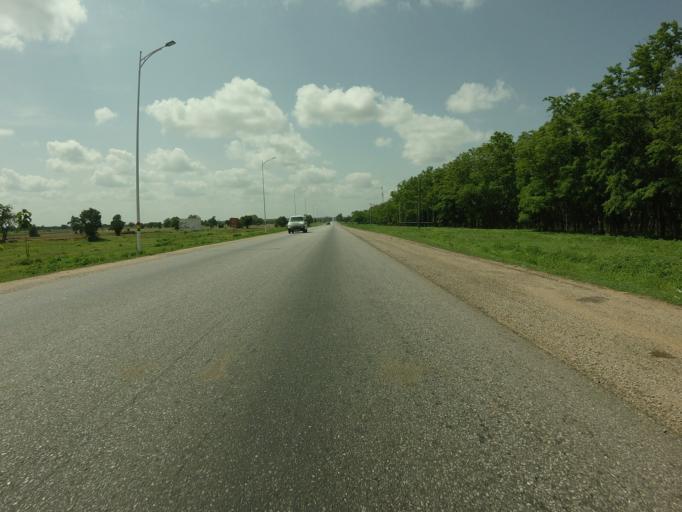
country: GH
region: Northern
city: Savelugu
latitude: 9.5407
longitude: -0.8391
